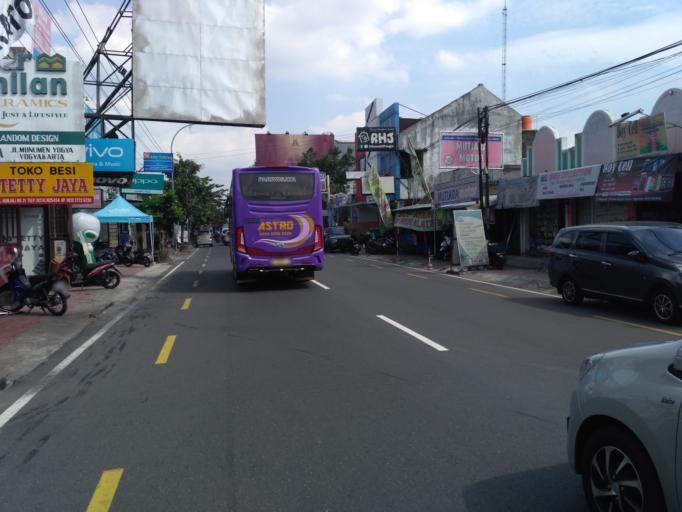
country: ID
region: Daerah Istimewa Yogyakarta
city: Melati
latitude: -7.7535
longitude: 110.3704
